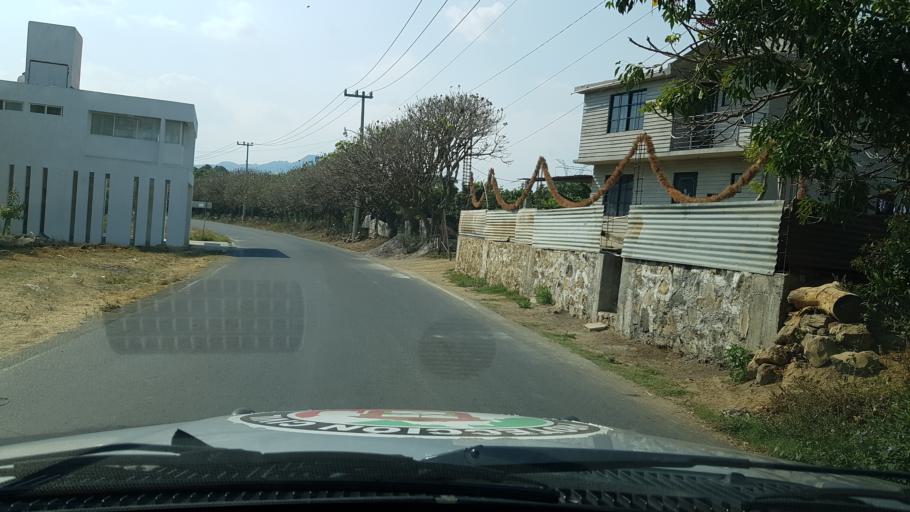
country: MX
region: Mexico
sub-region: Ozumba
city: San Jose Tlacotitlan
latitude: 18.9863
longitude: -98.8119
